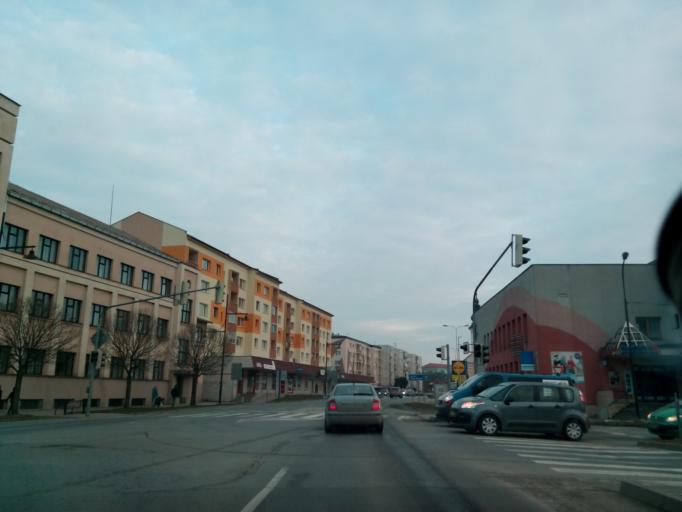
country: SK
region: Presovsky
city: Sabinov
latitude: 49.1018
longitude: 21.1001
